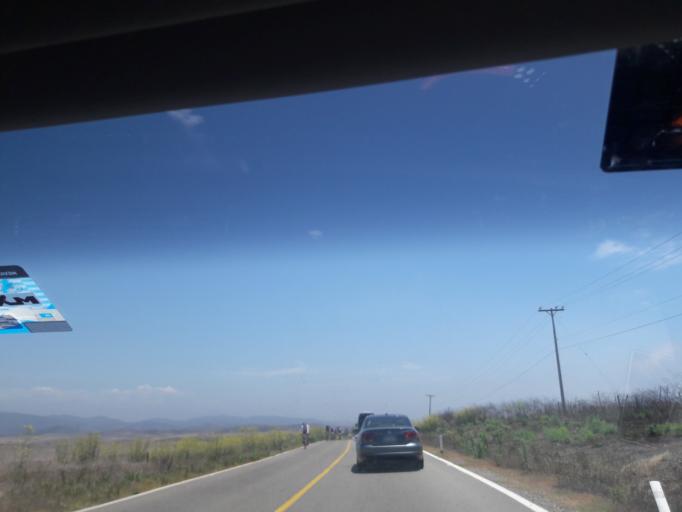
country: MX
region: Baja California
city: El Sauzal
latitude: 31.9841
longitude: -116.7436
